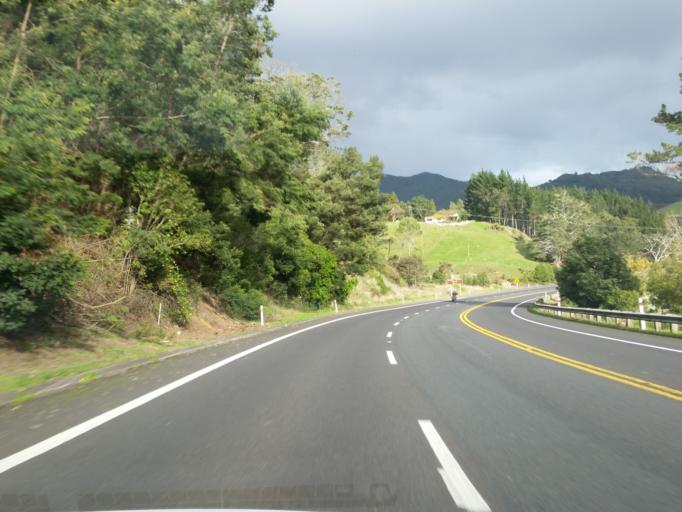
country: NZ
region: Waikato
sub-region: Hauraki District
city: Paeroa
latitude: -37.4038
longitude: 175.7080
